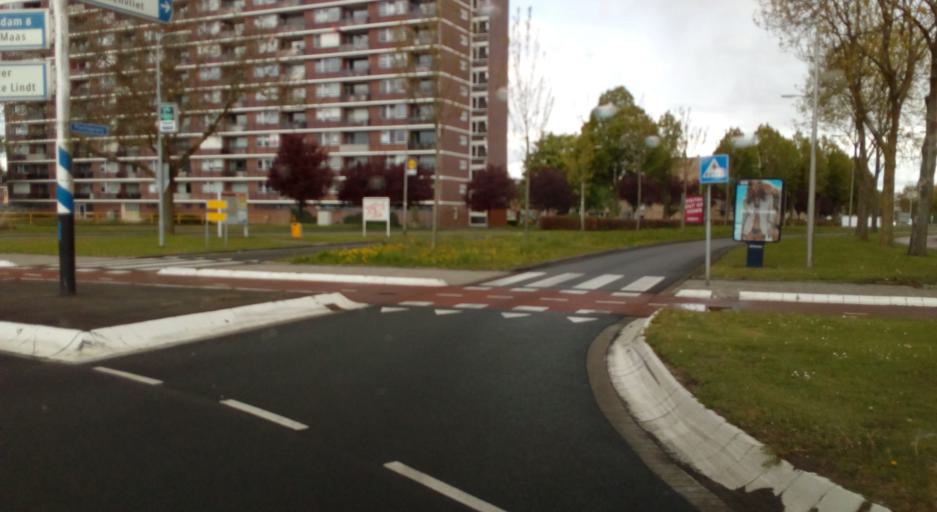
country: NL
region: South Holland
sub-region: Gemeente Zwijndrecht
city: Zwijndrecht
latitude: 51.8128
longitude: 4.6325
